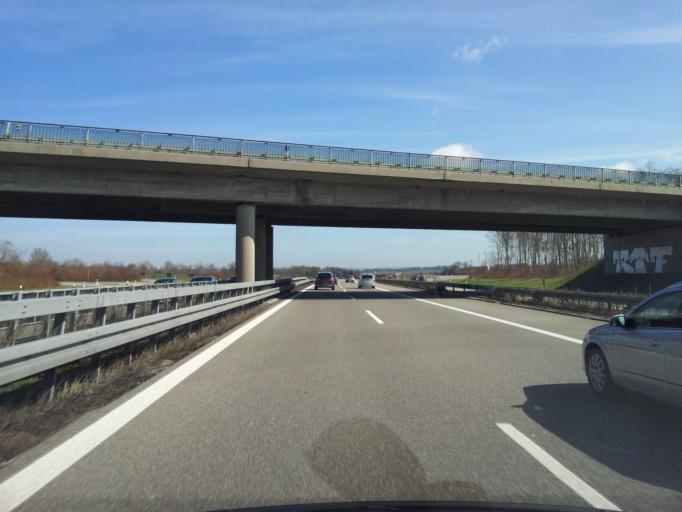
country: DE
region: Baden-Wuerttemberg
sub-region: Regierungsbezirk Stuttgart
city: Bondorf
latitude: 48.5026
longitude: 8.8418
